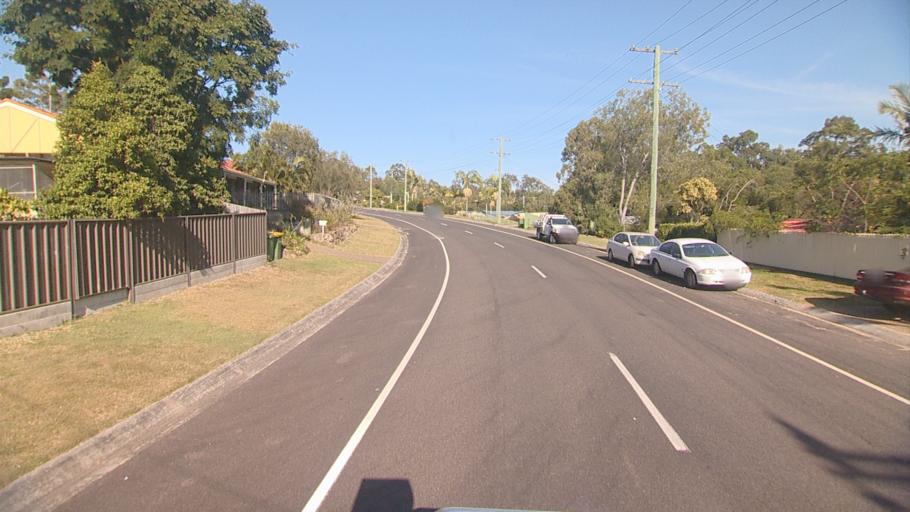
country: AU
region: Queensland
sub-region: Logan
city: Windaroo
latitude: -27.7204
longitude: 153.1820
